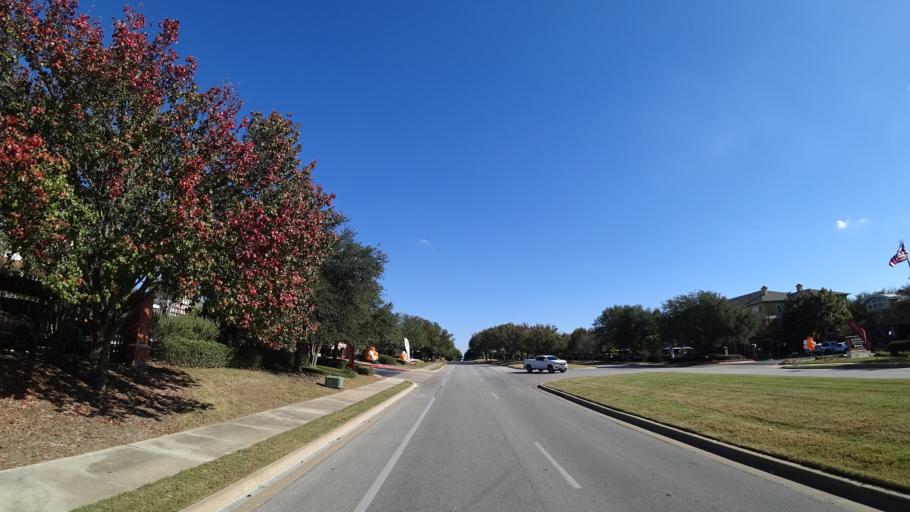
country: US
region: Texas
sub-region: Travis County
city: Wells Branch
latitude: 30.4299
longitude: -97.6972
